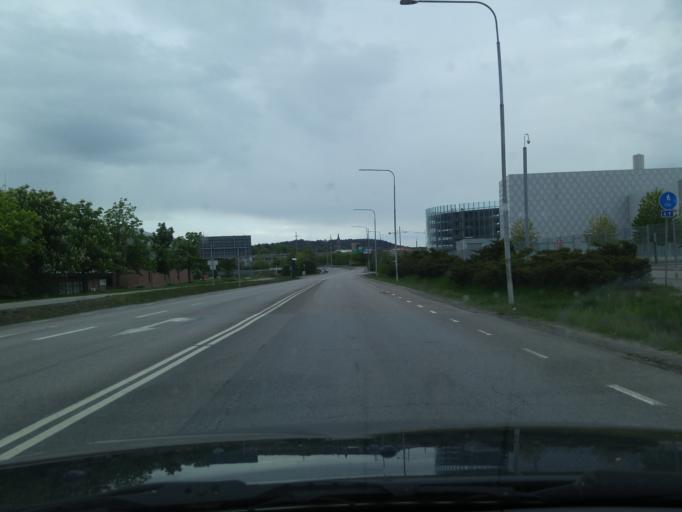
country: SE
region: Vaestra Goetaland
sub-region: Molndal
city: Moelndal
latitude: 57.6423
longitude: 12.0184
